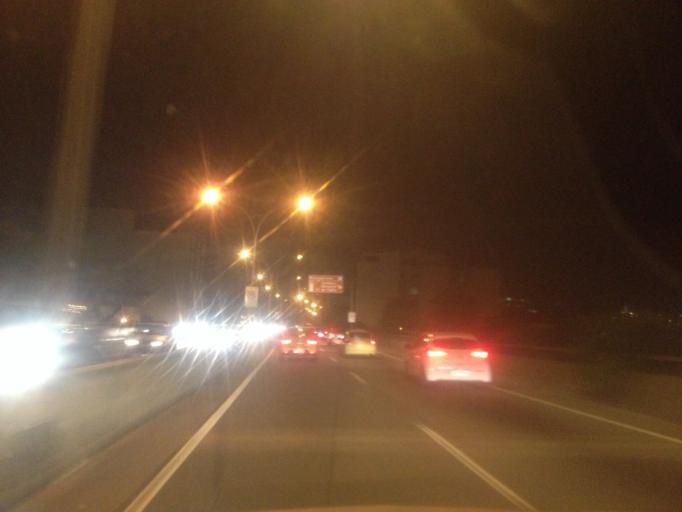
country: BR
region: Rio de Janeiro
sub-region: Rio De Janeiro
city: Rio de Janeiro
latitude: -22.9167
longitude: -43.2101
